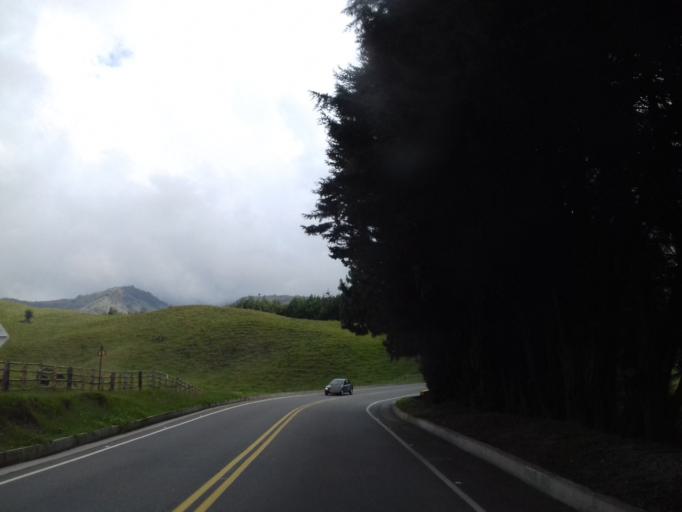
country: CO
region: Caldas
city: Villamaria
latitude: 5.0157
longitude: -75.3551
